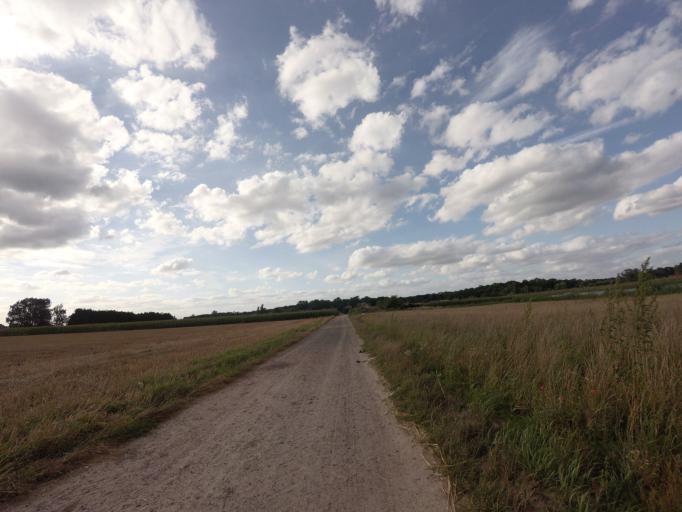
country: BE
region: Flanders
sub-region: Provincie Vlaams-Brabant
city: Grimbergen
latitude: 50.9710
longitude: 4.3737
